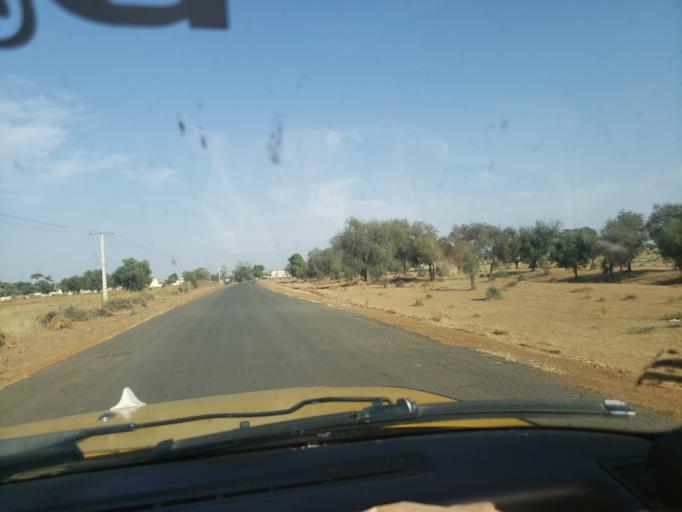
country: SN
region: Louga
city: Louga
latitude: 15.5126
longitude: -15.9997
